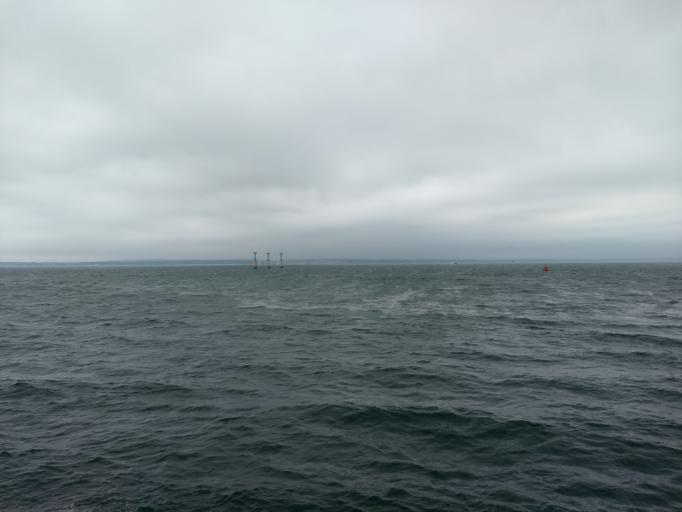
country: GB
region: England
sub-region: Portsmouth
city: Southsea
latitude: 50.7791
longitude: -1.0981
